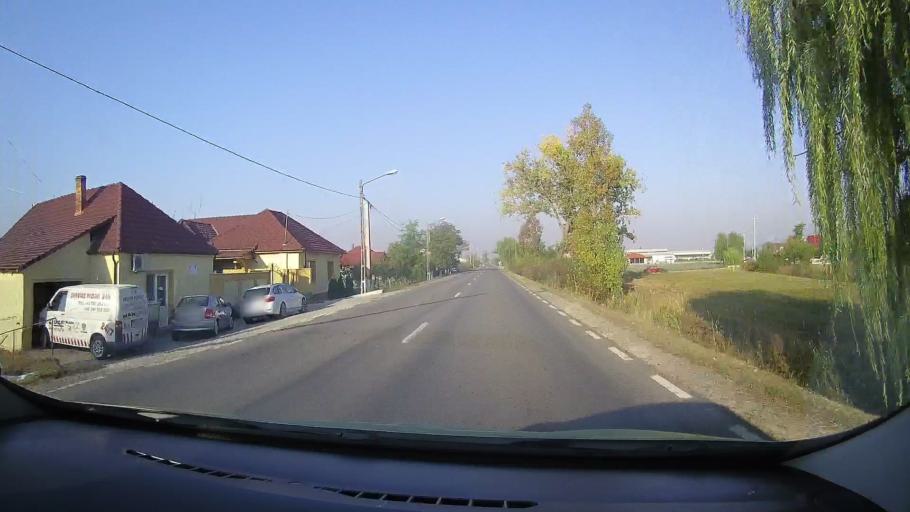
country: RO
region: Arad
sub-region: Comuna Socodor
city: Socodor
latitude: 46.5007
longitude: 21.4368
